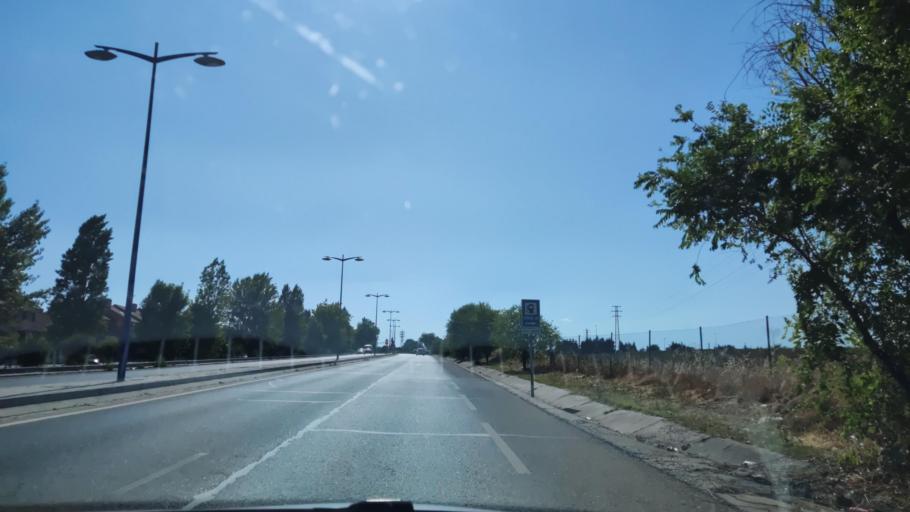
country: ES
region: Madrid
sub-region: Provincia de Madrid
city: Leganes
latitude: 40.3466
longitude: -3.7667
